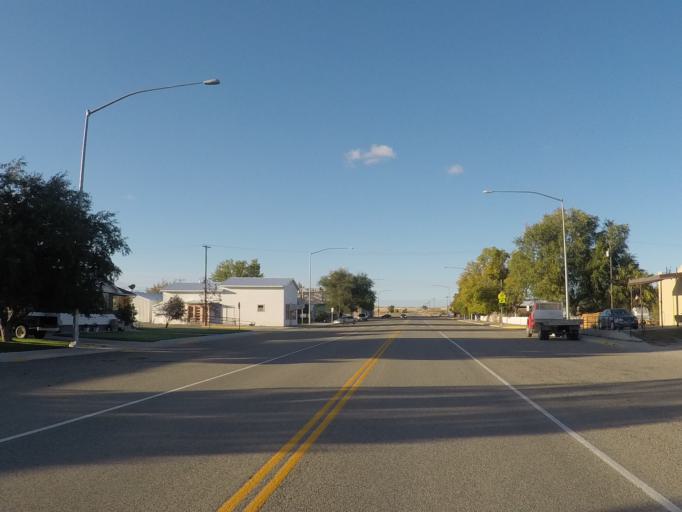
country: US
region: Montana
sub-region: Golden Valley County
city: Ryegate
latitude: 46.2930
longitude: -108.9379
